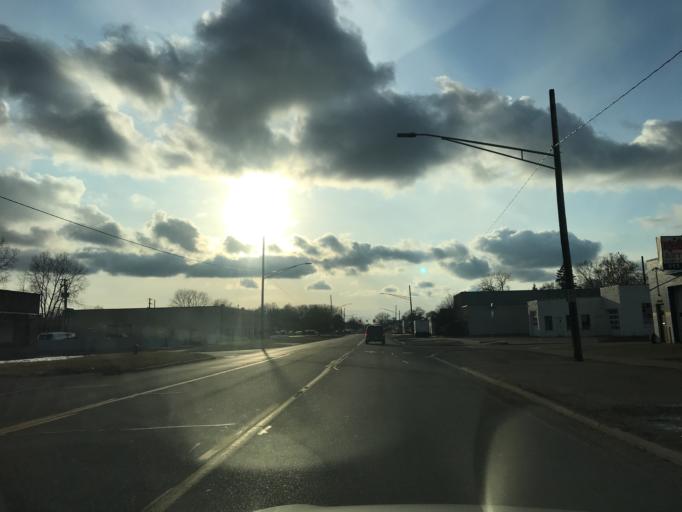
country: US
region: Michigan
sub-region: Wayne County
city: Redford
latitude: 42.4283
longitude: -83.2999
